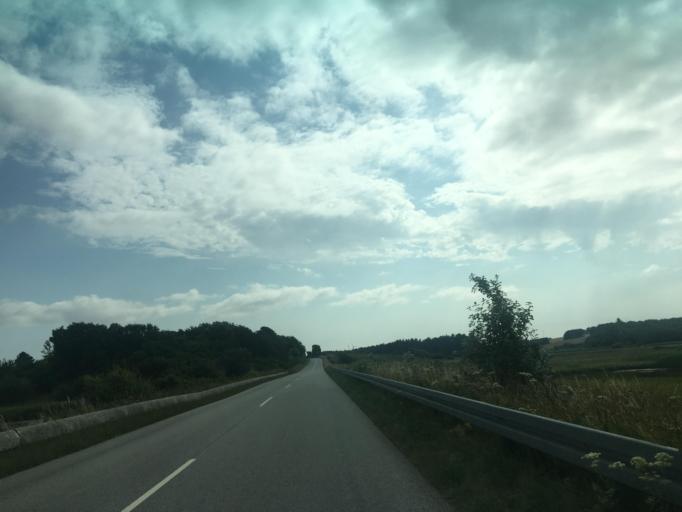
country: DK
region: North Denmark
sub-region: Thisted Kommune
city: Thisted
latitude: 56.8713
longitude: 8.6233
